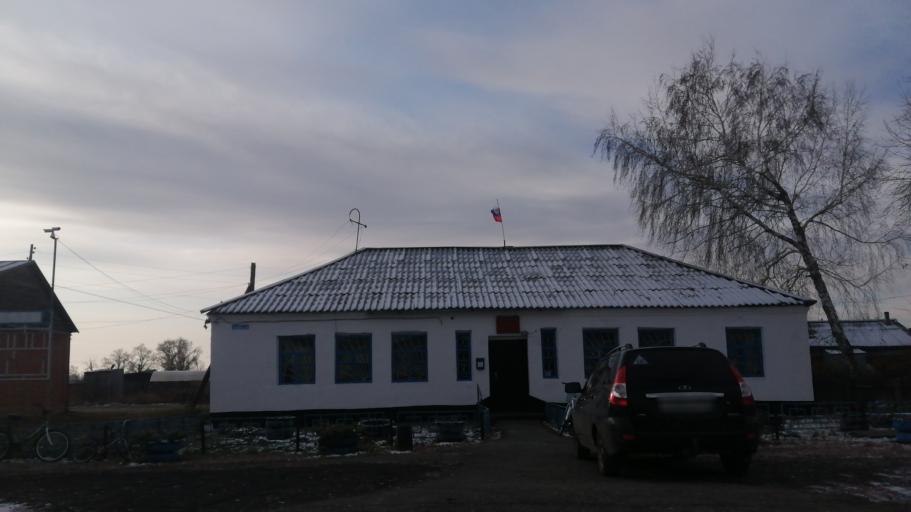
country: RU
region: Altai Krai
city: Ust'yanka
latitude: 53.9850
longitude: 78.7009
